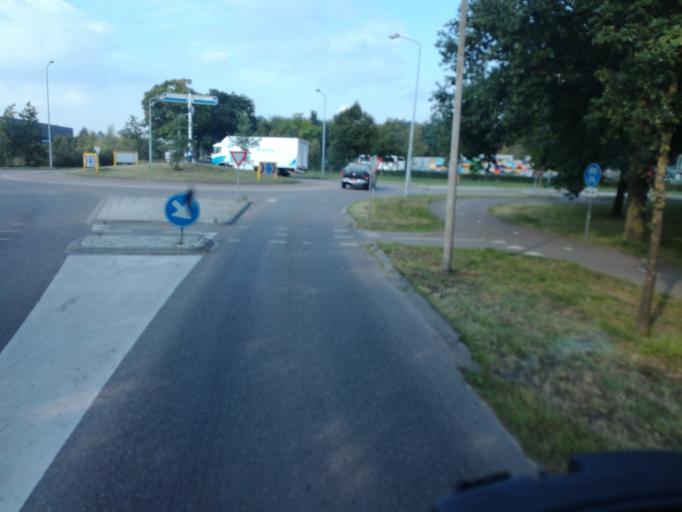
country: NL
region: North Brabant
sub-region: Gemeente Uden
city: Volkel
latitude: 51.6551
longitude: 5.6732
